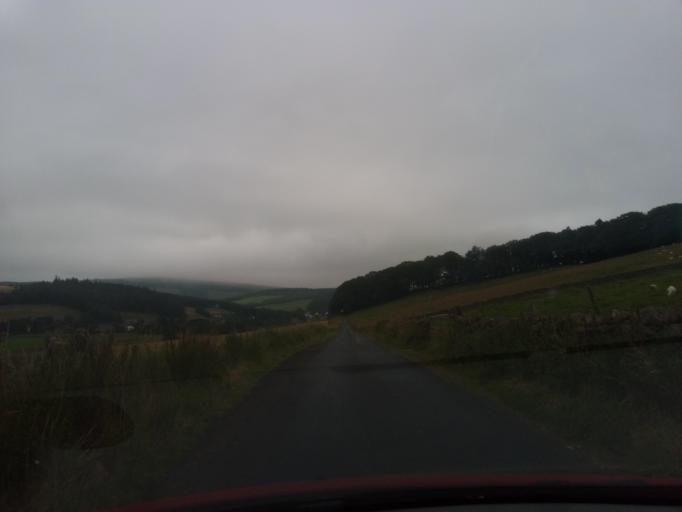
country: GB
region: Scotland
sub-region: The Scottish Borders
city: Galashiels
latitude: 55.6965
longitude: -2.8769
